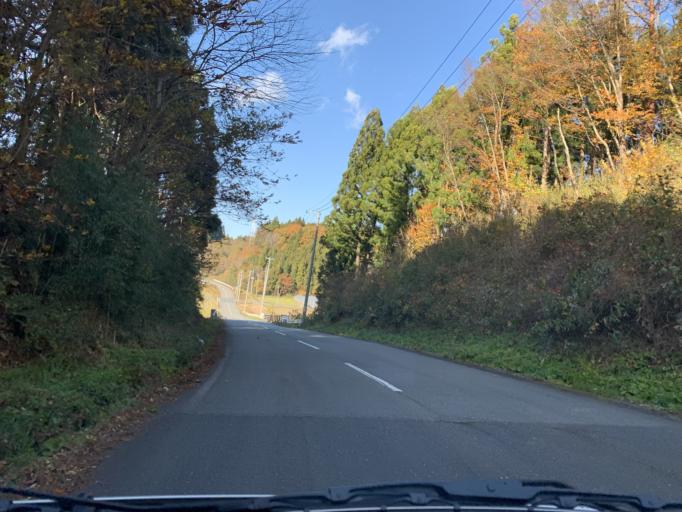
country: JP
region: Iwate
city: Mizusawa
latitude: 39.0904
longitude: 141.1258
